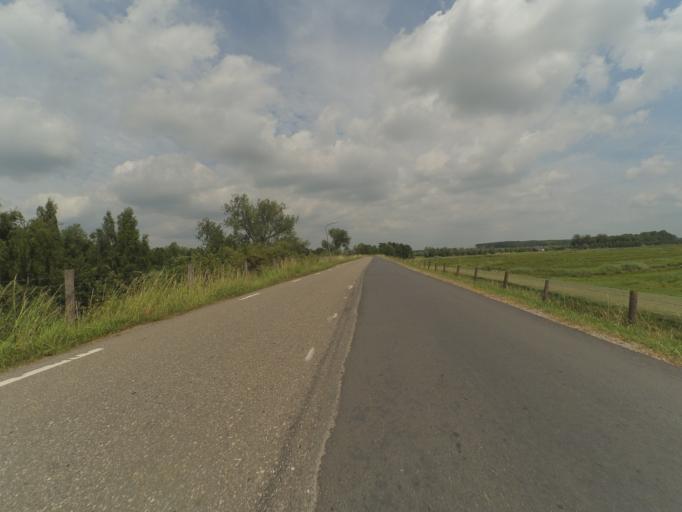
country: NL
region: South Holland
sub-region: Gemeente Leerdam
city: Leerdam
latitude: 51.9288
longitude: 5.1472
